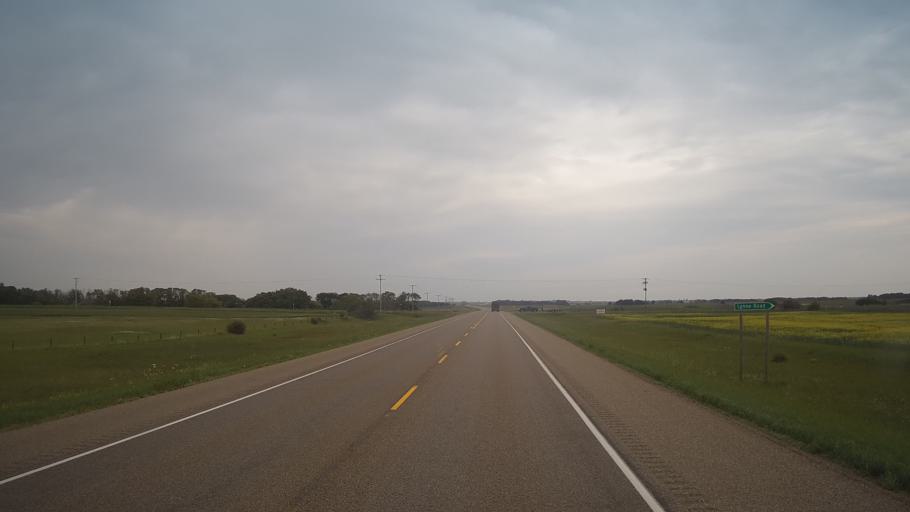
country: CA
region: Saskatchewan
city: Langham
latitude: 52.1294
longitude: -107.0950
